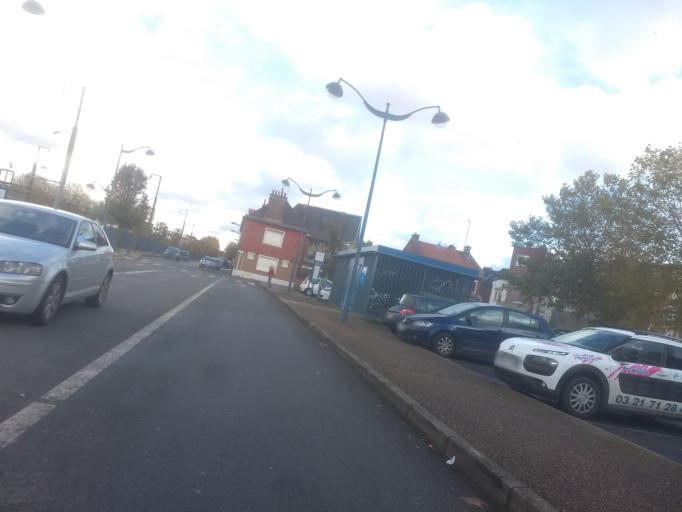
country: FR
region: Nord-Pas-de-Calais
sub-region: Departement du Pas-de-Calais
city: Arras
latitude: 50.2863
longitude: 2.7820
